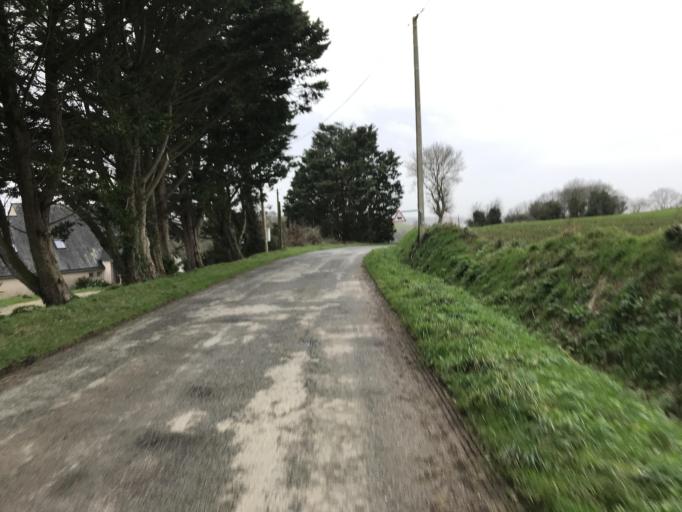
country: FR
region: Brittany
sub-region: Departement du Finistere
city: Daoulas
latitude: 48.3572
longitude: -4.2777
